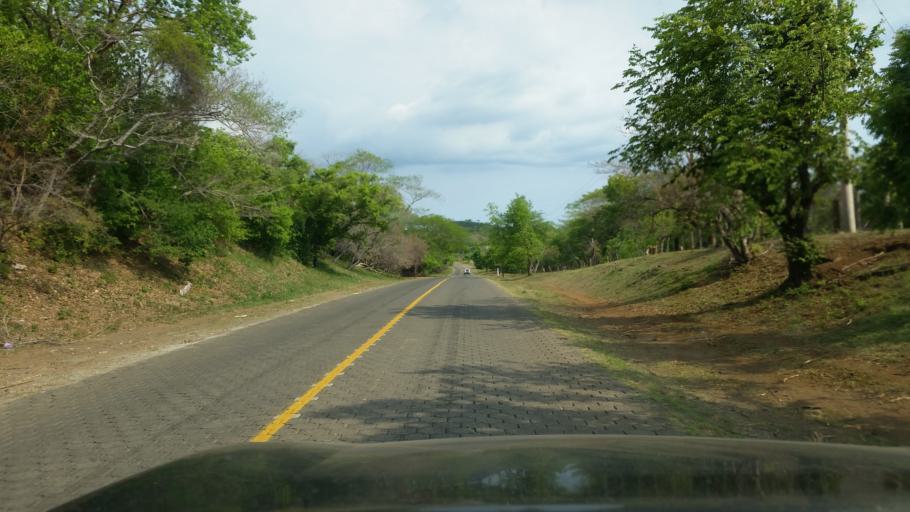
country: NI
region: Managua
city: Masachapa
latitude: 11.8485
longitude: -86.5169
